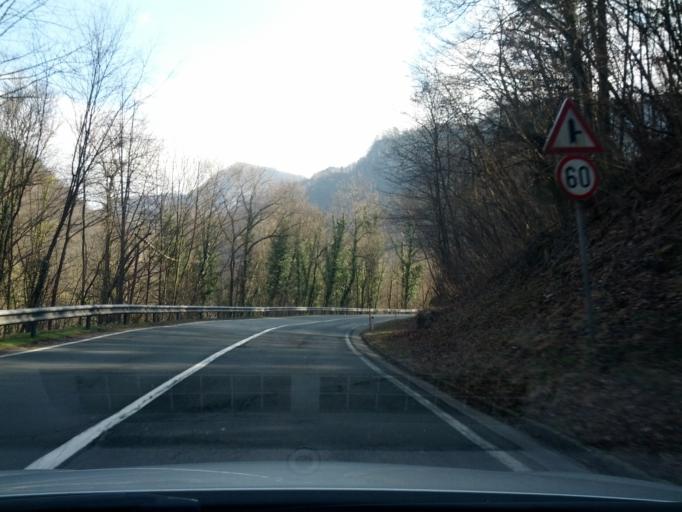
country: SI
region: Zagorje ob Savi
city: Kisovec
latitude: 46.0911
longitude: 14.9436
